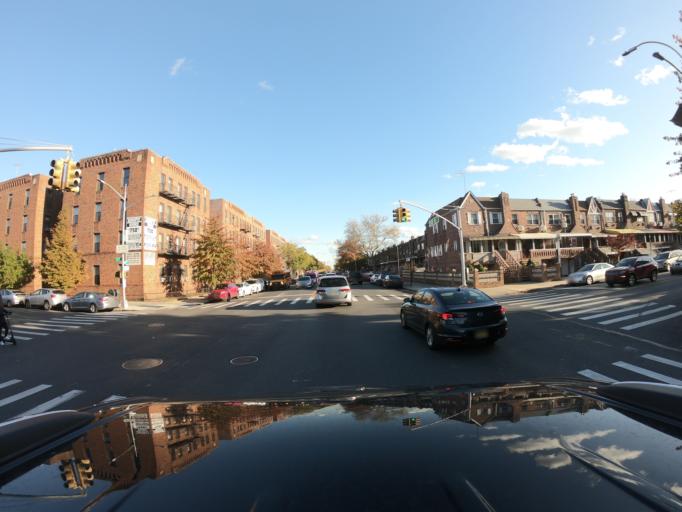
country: US
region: New York
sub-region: Kings County
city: Bensonhurst
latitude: 40.6221
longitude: -73.9951
